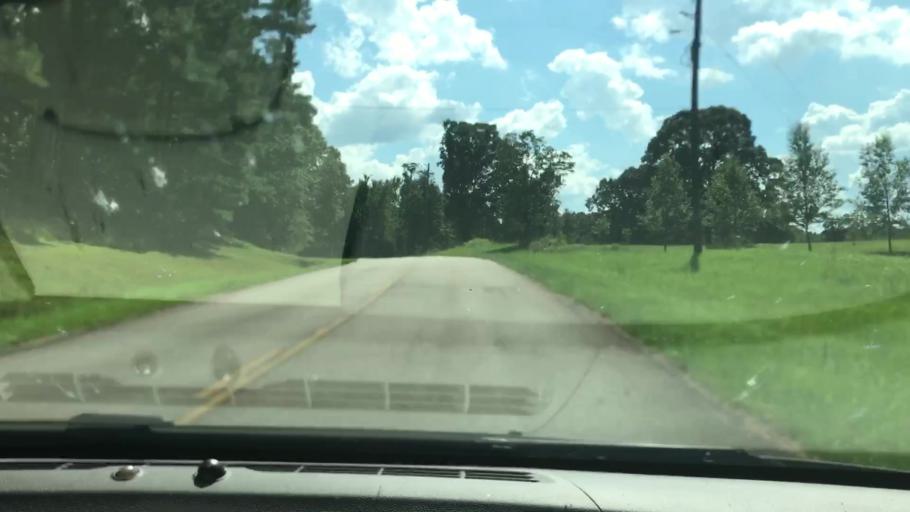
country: US
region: Georgia
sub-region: Troup County
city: La Grange
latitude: 33.1106
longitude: -85.1274
